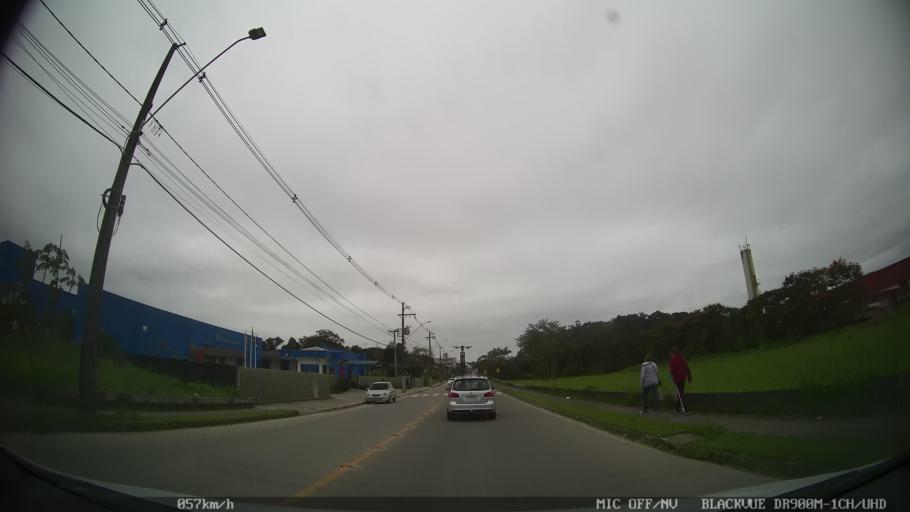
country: BR
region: Santa Catarina
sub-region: Joinville
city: Joinville
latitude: -26.2774
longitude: -48.9070
